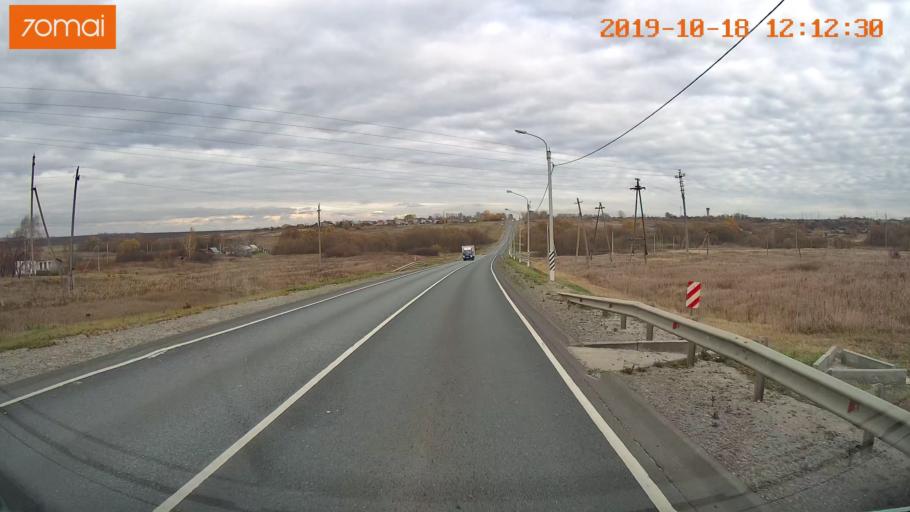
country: RU
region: Rjazan
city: Zakharovo
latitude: 54.4122
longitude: 39.3589
